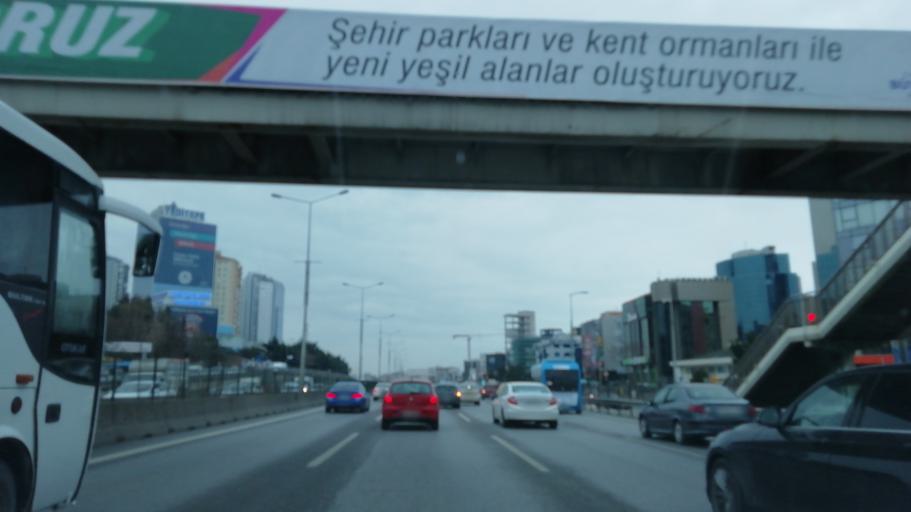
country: TR
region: Istanbul
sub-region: Atasehir
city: Atasehir
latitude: 40.9706
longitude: 29.1015
